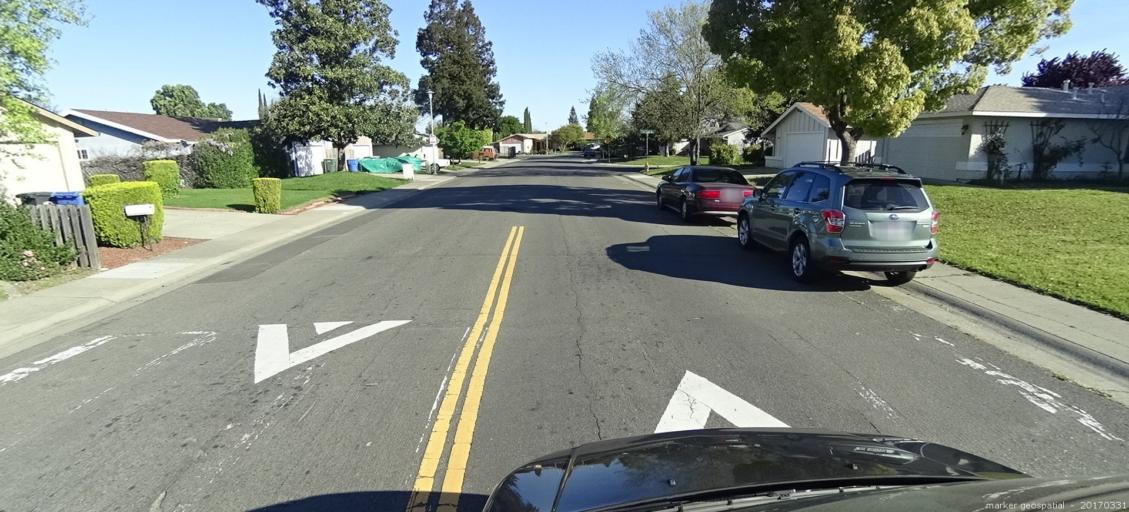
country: US
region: California
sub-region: Sacramento County
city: Parkway
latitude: 38.4691
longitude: -121.4578
